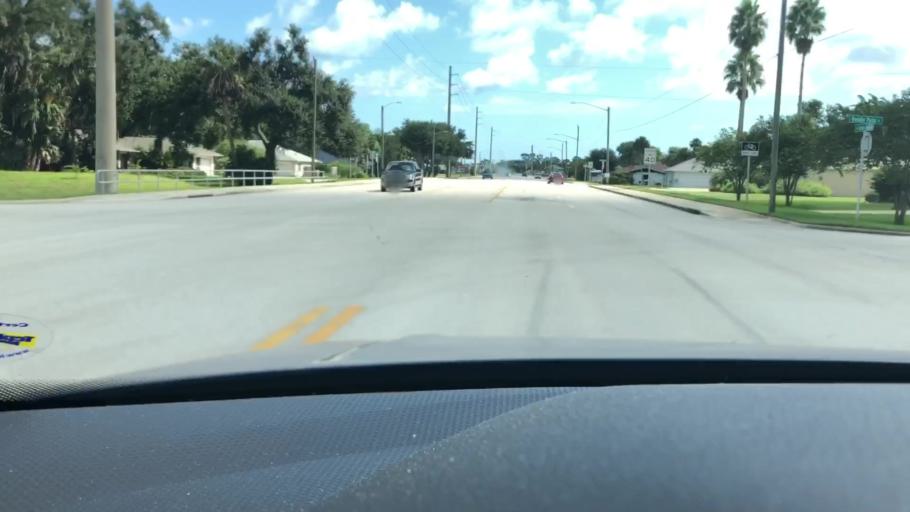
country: US
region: Florida
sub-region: Volusia County
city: Edgewater
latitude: 28.9676
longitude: -80.9081
